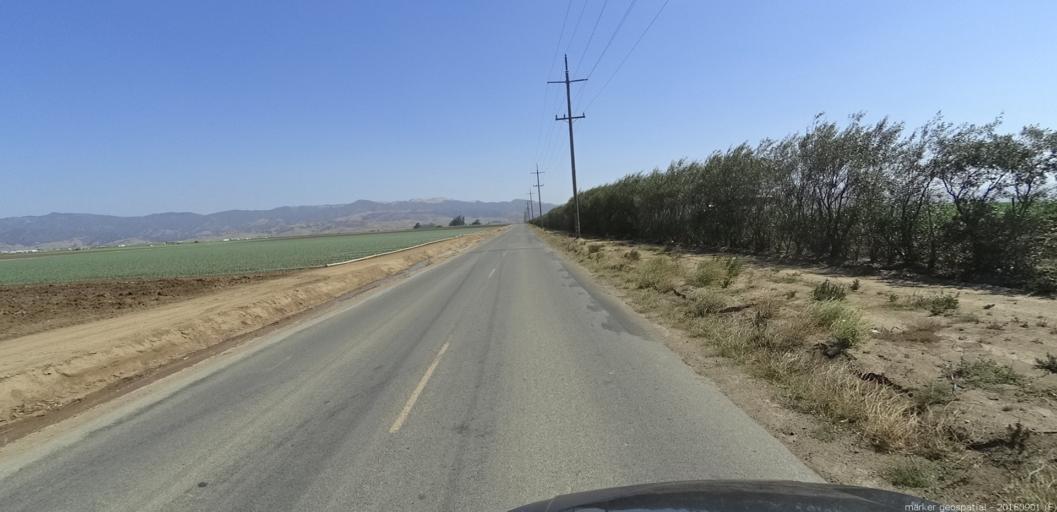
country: US
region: California
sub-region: Monterey County
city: Chualar
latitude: 36.5767
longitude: -121.5099
